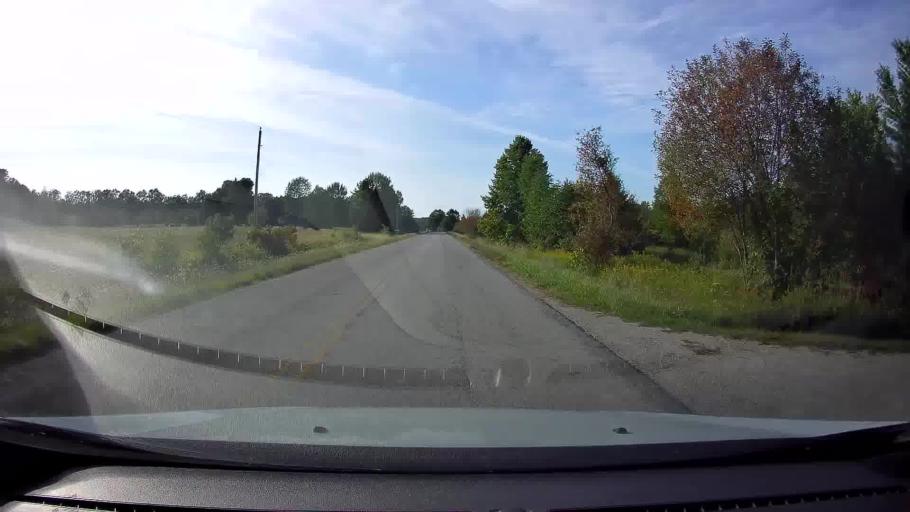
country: US
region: Wisconsin
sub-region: Door County
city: Sturgeon Bay
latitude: 45.1713
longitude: -87.1332
